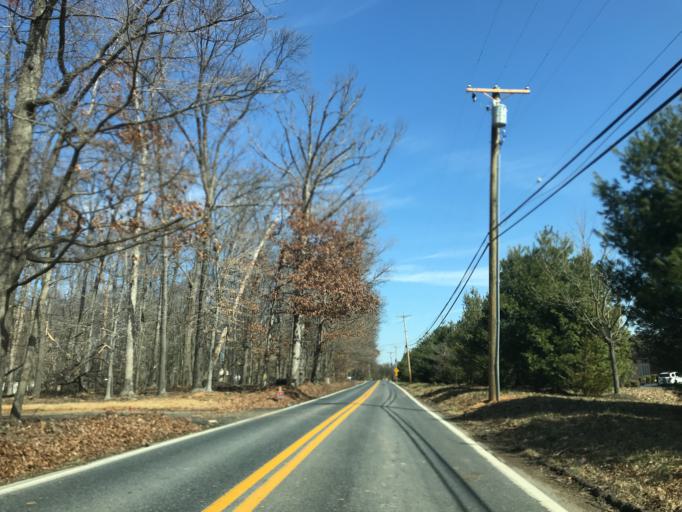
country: US
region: Maryland
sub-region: Howard County
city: Highland
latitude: 39.1833
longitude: -76.9309
